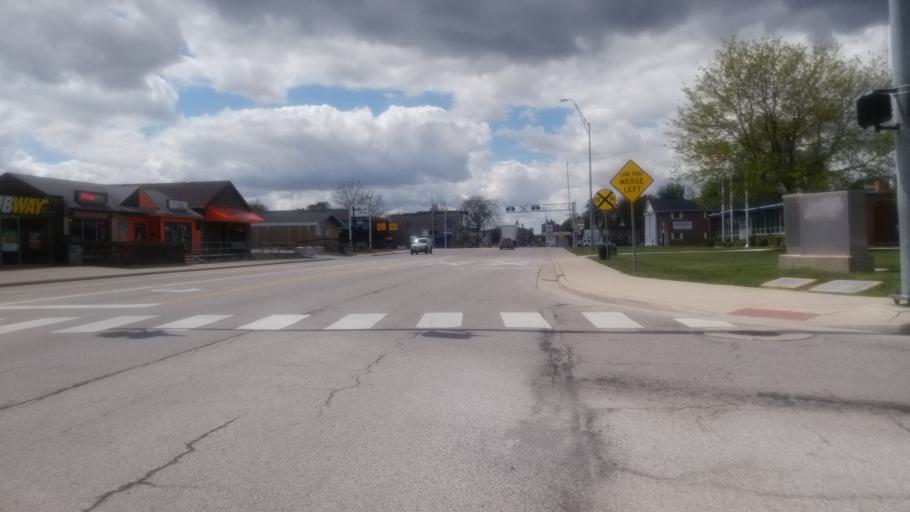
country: US
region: Ohio
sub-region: Wood County
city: Bowling Green
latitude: 41.3749
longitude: -83.6432
